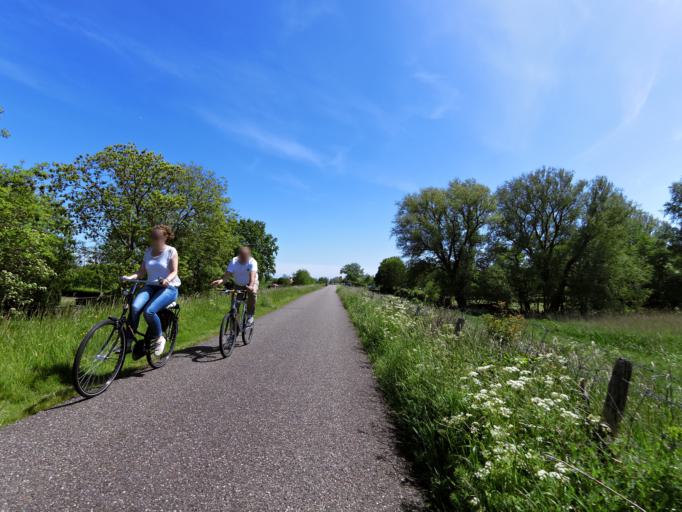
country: NL
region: South Holland
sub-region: Gemeente Hellevoetsluis
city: Nieuw-Helvoet
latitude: 51.8324
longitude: 4.0922
